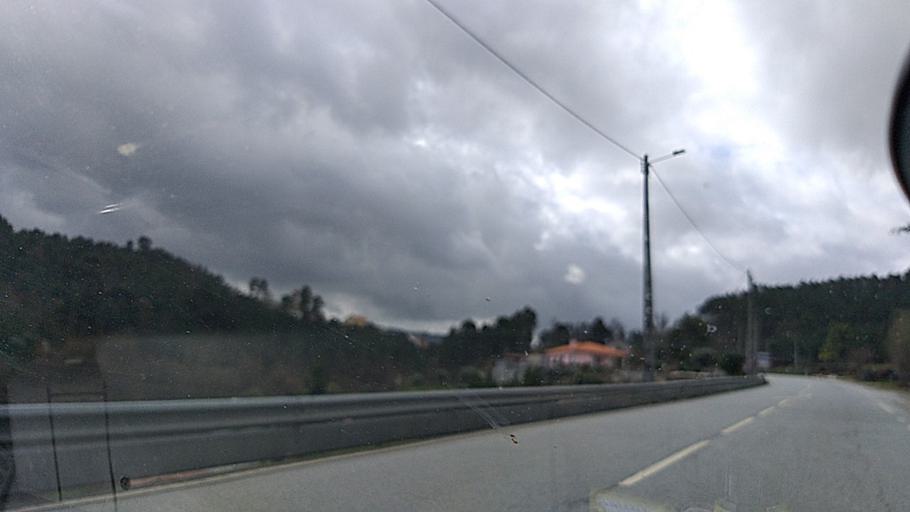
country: PT
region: Viseu
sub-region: Mangualde
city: Mangualde
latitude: 40.6422
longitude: -7.7381
